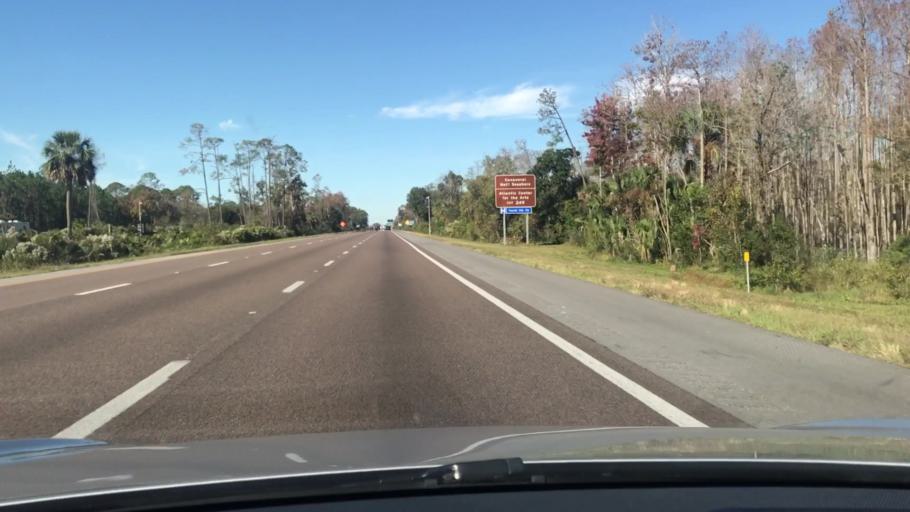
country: US
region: Florida
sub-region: Volusia County
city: Glencoe
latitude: 28.9980
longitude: -80.9778
